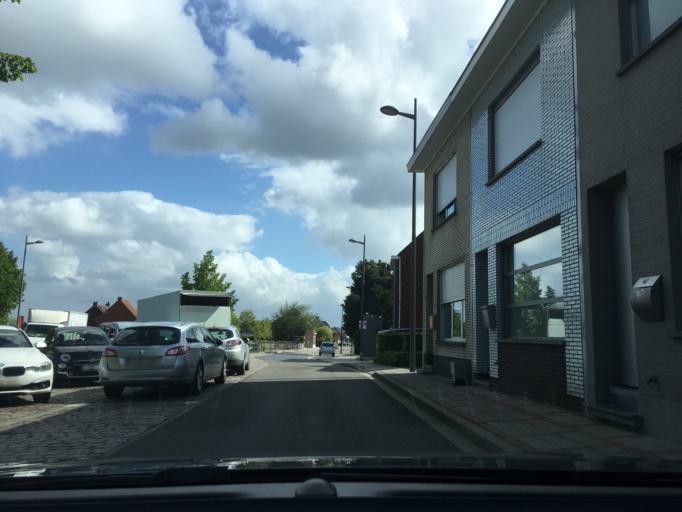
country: BE
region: Flanders
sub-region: Provincie West-Vlaanderen
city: Tielt
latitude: 51.0024
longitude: 3.3303
